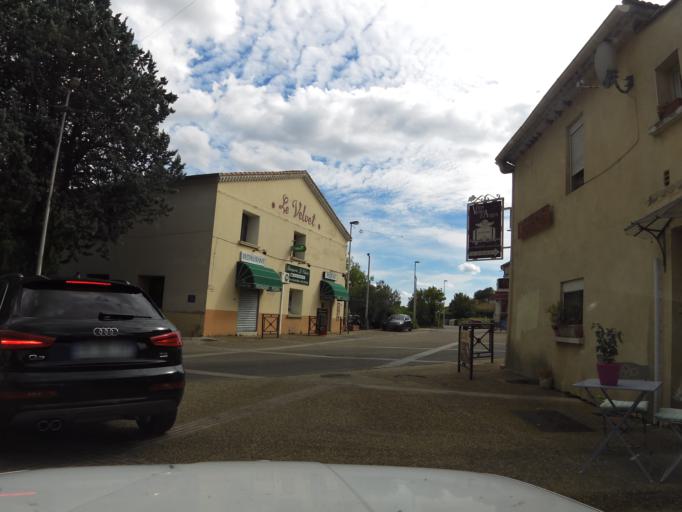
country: FR
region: Languedoc-Roussillon
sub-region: Departement du Gard
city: Bagard
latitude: 44.0723
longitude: 4.0511
